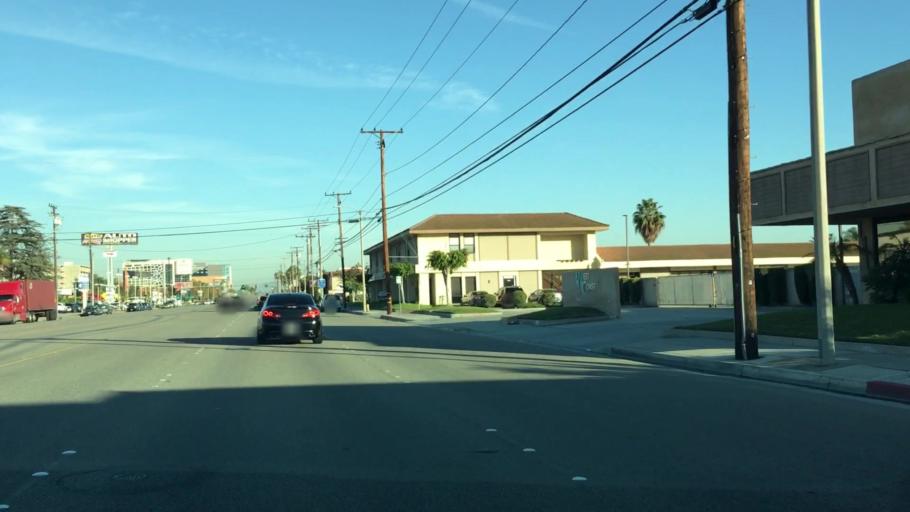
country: US
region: California
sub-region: Orange County
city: Buena Park
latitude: 33.8590
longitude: -118.0057
